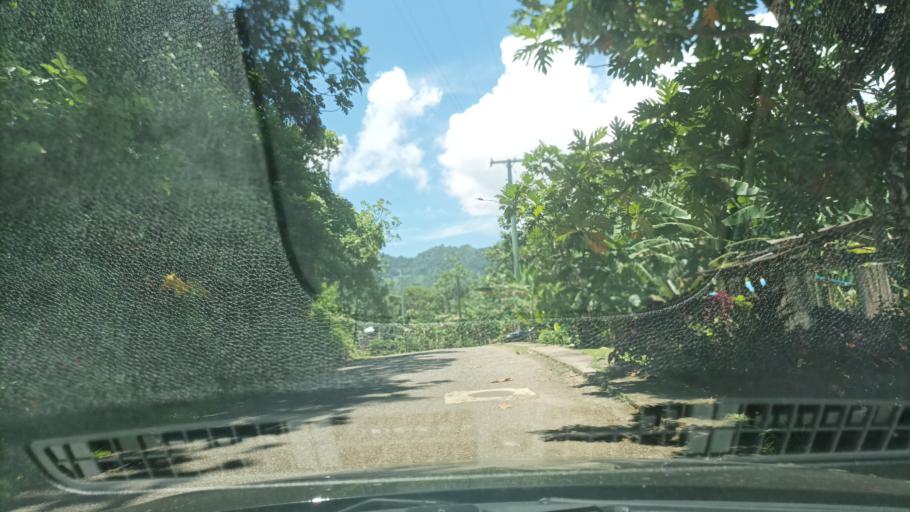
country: FM
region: Kosrae
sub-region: Lelu Municipality
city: Lelu
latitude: 5.3316
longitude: 163.0267
